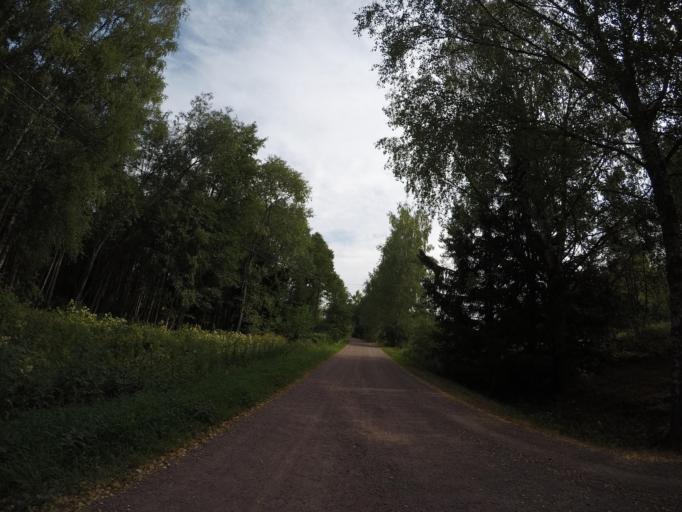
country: AX
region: Alands landsbygd
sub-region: Finstroem
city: Finstroem
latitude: 60.2265
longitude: 19.8487
